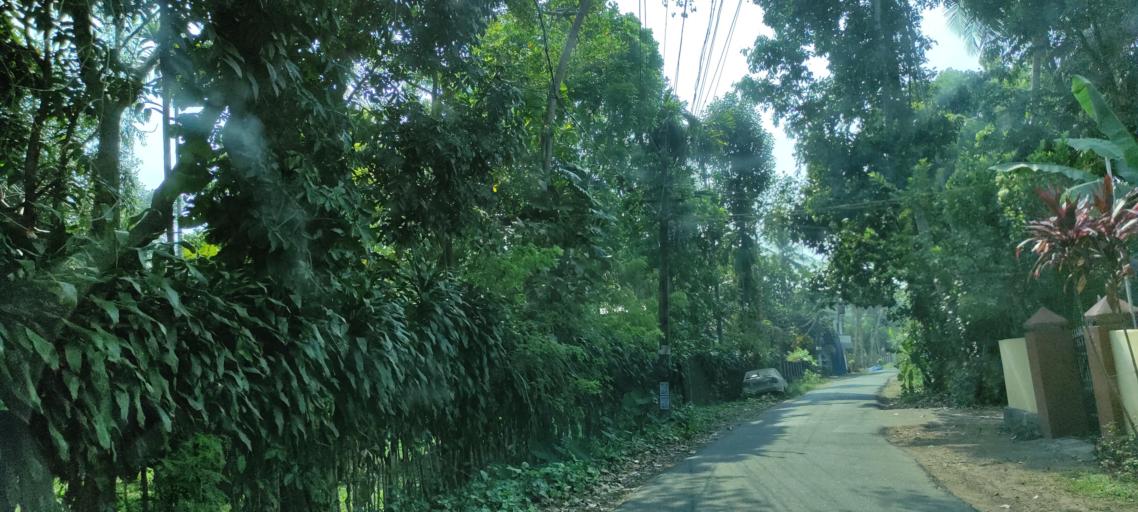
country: IN
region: Kerala
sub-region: Pattanamtitta
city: Tiruvalla
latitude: 9.3445
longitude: 76.5419
